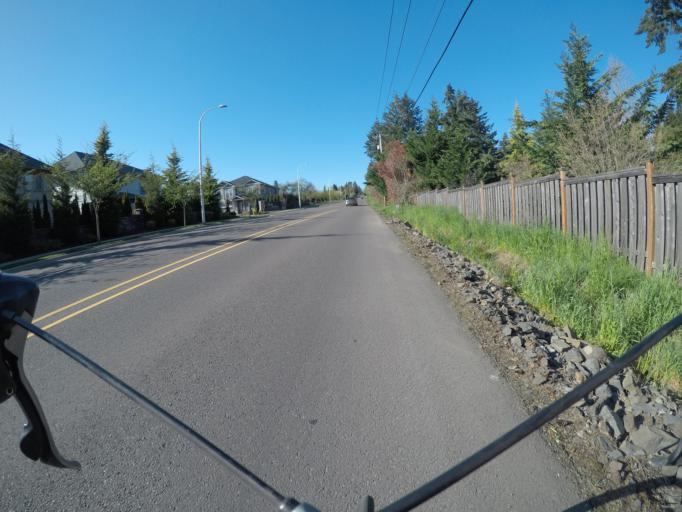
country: US
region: Oregon
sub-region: Washington County
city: King City
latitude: 45.4092
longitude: -122.8313
